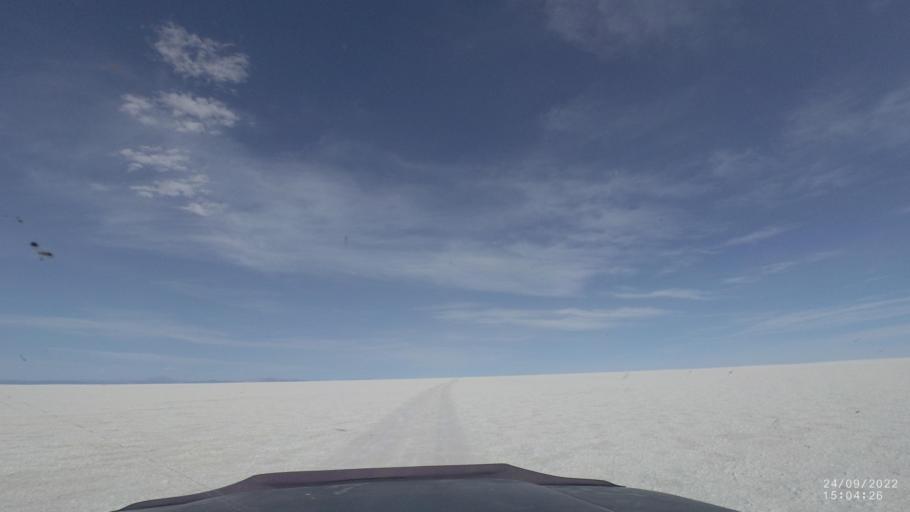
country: BO
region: Potosi
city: Colchani
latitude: -19.9001
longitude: -67.5243
